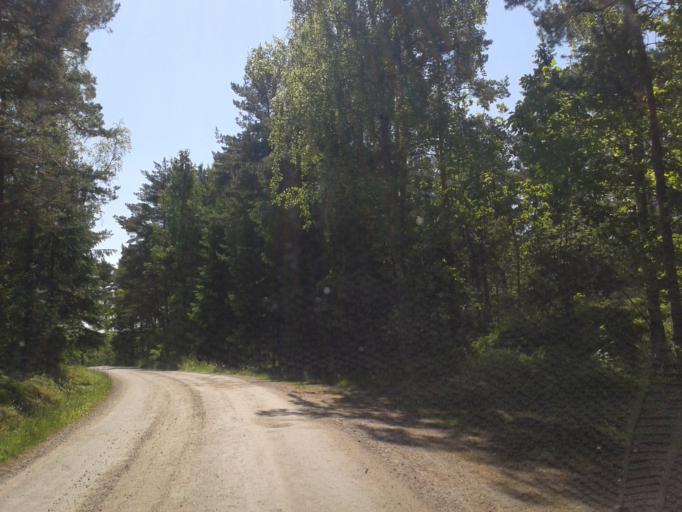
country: SE
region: Vaestra Goetaland
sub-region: Stromstads Kommun
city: Stroemstad
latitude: 58.8605
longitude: 11.2281
